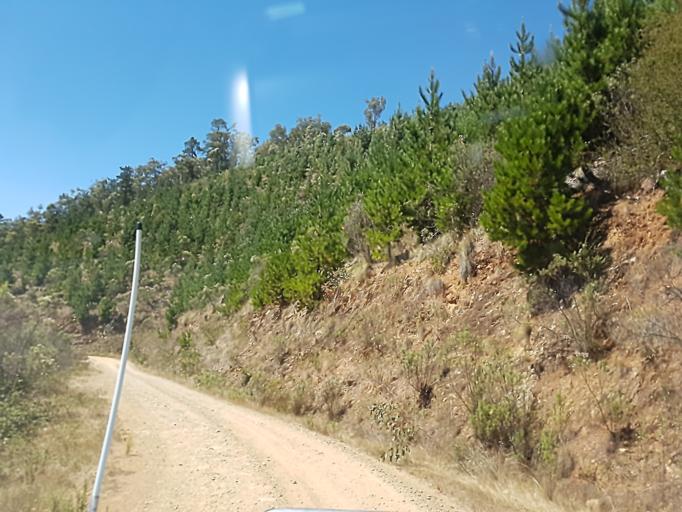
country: AU
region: Victoria
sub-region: Alpine
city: Mount Beauty
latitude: -36.7420
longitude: 146.9608
